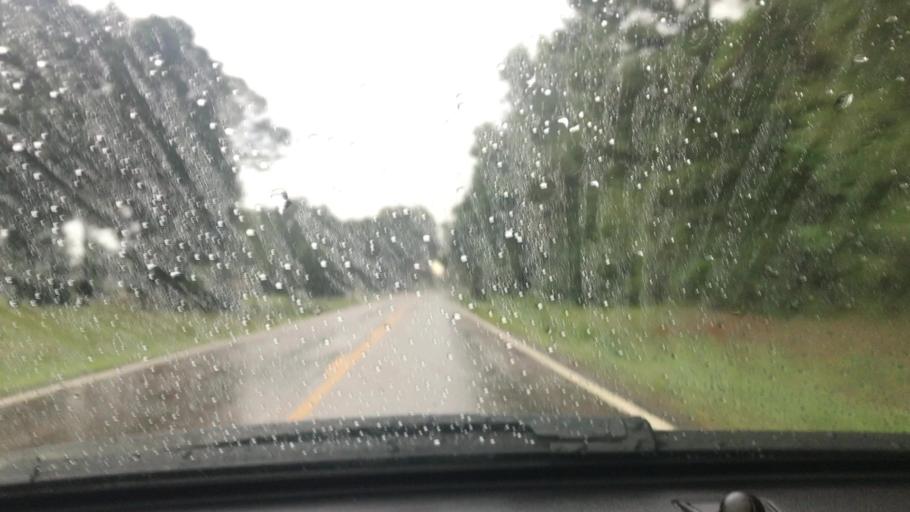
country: US
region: Mississippi
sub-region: Pike County
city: Summit
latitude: 31.3178
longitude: -90.5297
